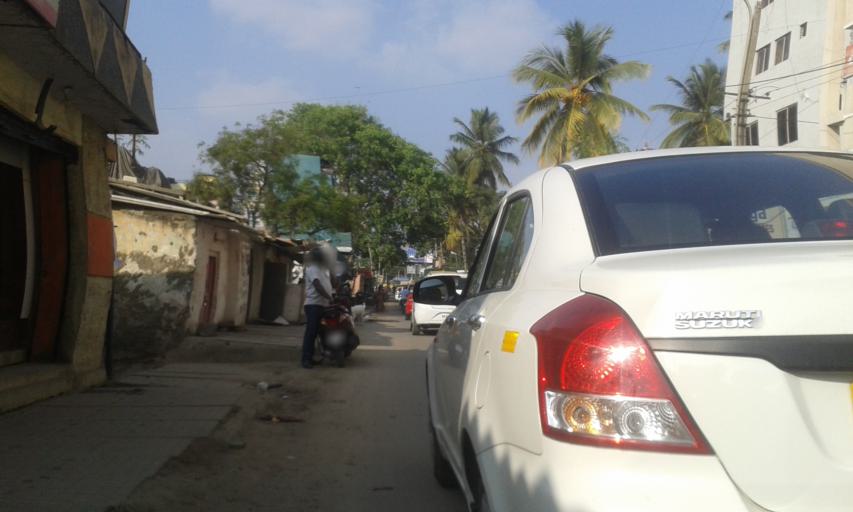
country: IN
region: Karnataka
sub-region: Bangalore Urban
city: Bangalore
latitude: 12.9530
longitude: 77.6203
